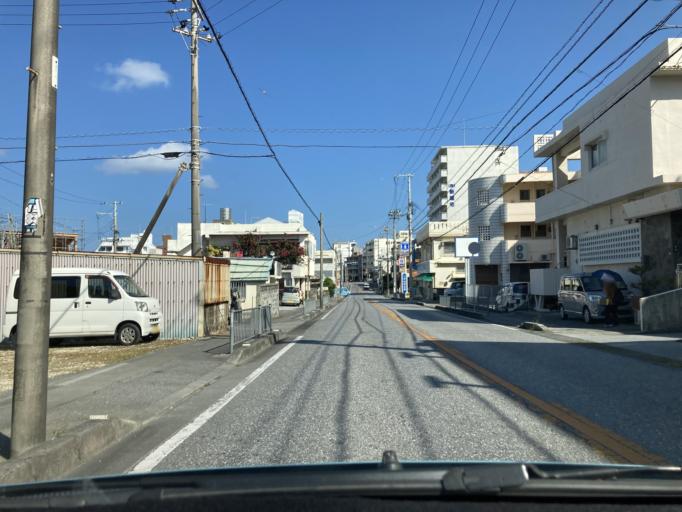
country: JP
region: Okinawa
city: Tomigusuku
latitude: 26.1874
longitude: 127.6598
